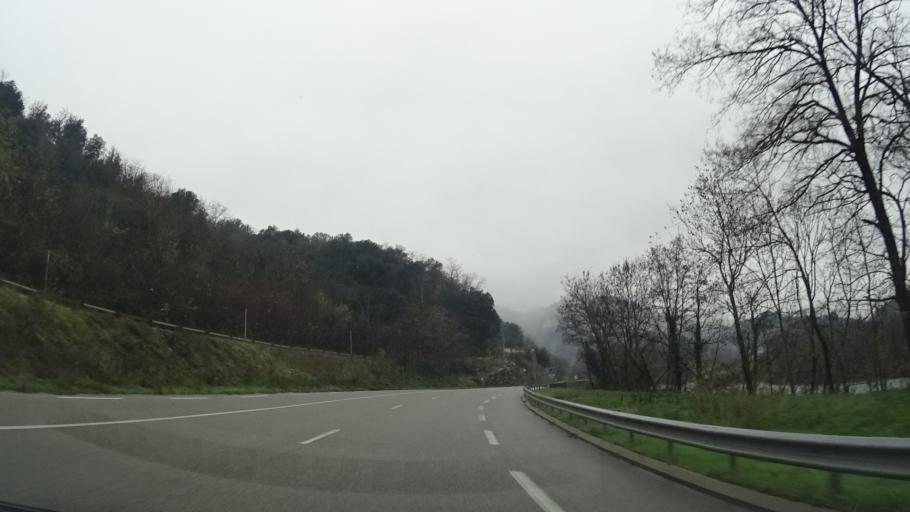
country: FR
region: Rhone-Alpes
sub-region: Departement de l'Ardeche
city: Jaujac
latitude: 44.6559
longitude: 4.3035
